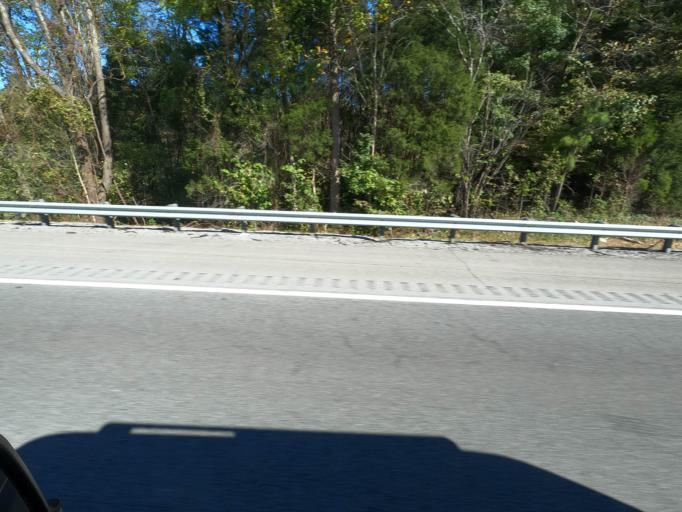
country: US
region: Tennessee
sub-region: Dickson County
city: Burns
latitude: 36.0187
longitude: -87.2537
